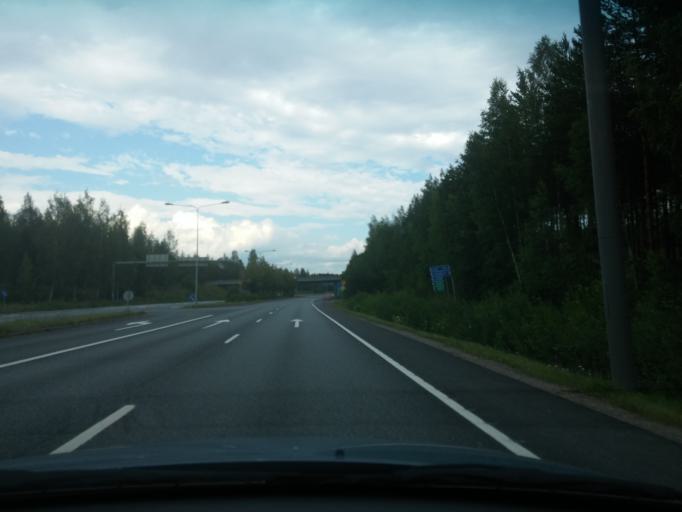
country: FI
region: Haeme
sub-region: Riihimaeki
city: Riihimaeki
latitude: 60.7491
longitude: 24.7215
